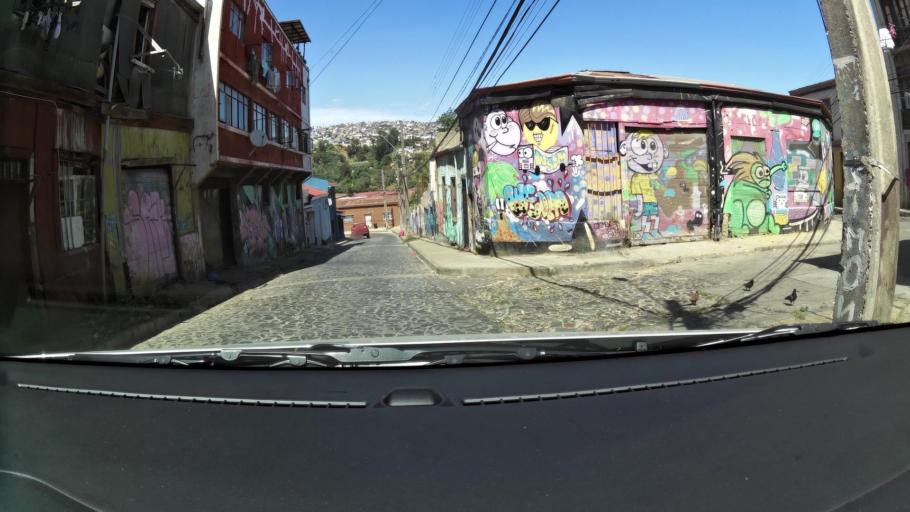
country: CL
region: Valparaiso
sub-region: Provincia de Valparaiso
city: Valparaiso
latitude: -33.0514
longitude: -71.5995
